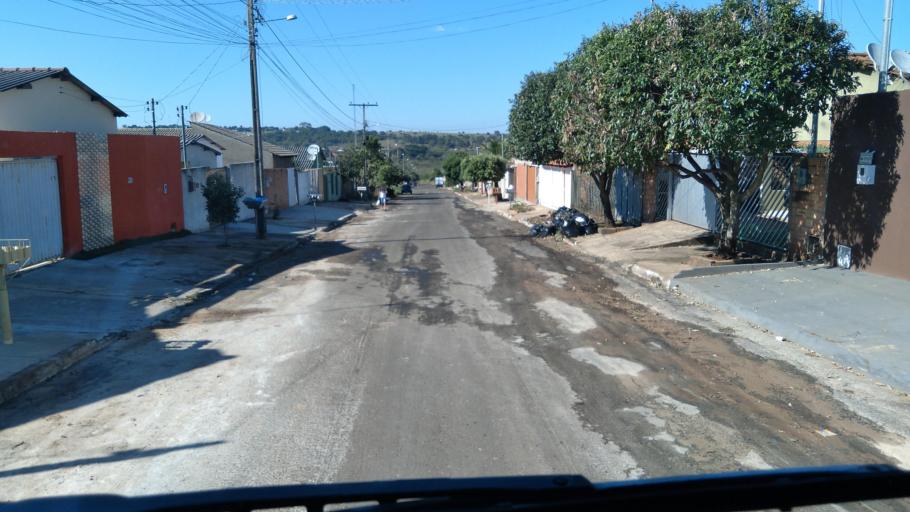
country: BR
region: Goias
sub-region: Mineiros
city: Mineiros
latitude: -17.5759
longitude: -52.5711
